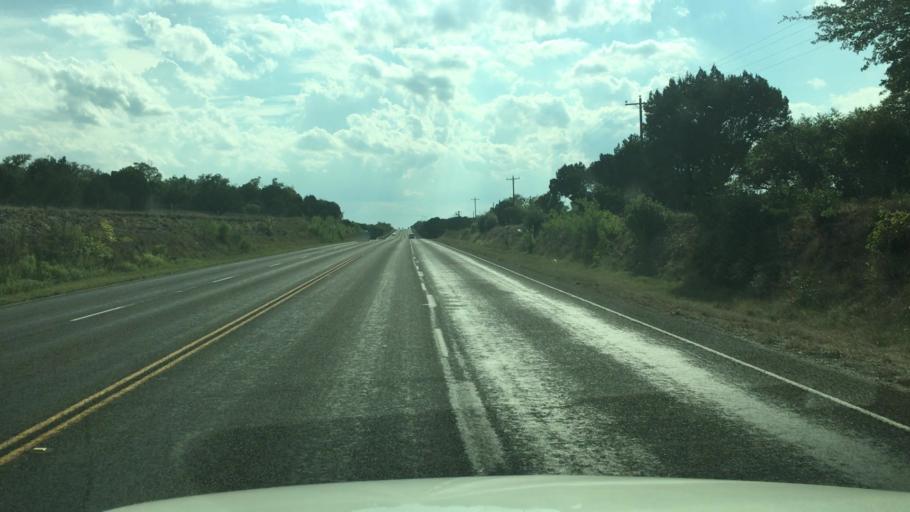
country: US
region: Texas
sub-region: Blanco County
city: Johnson City
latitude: 30.2103
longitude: -98.2876
